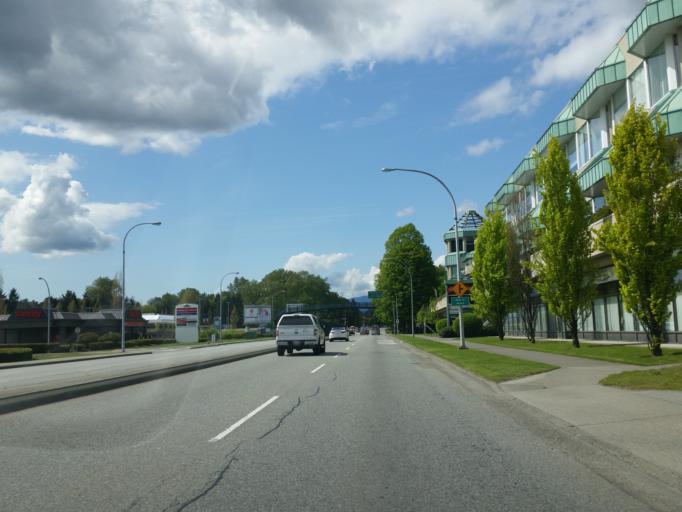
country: CA
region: British Columbia
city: Coquitlam
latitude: 49.2660
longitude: -122.7727
